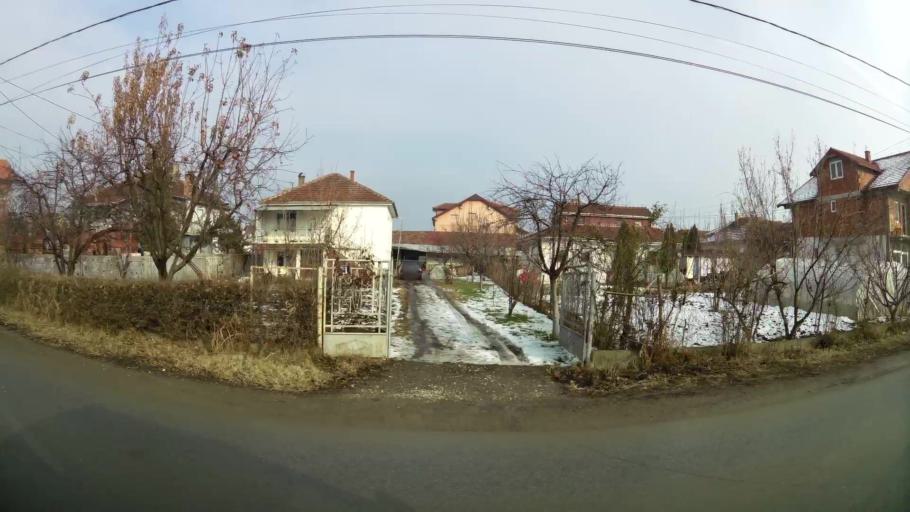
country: MK
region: Ilinden
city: Marino
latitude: 41.9939
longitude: 21.5885
